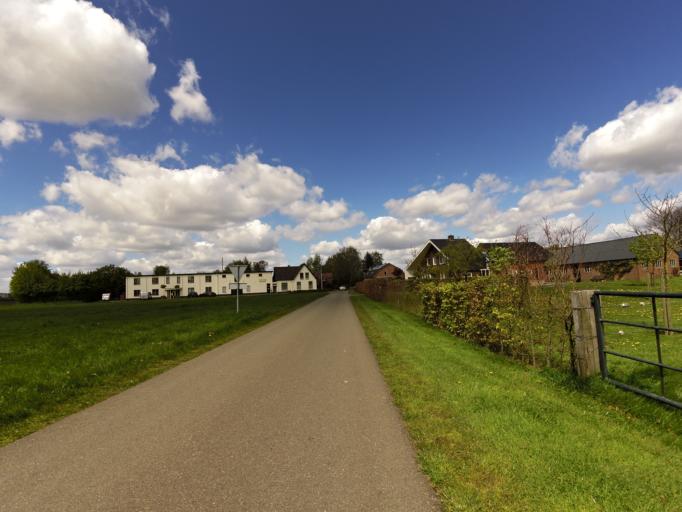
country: NL
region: Gelderland
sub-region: Gemeente Doetinchem
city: Doetinchem
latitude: 51.9408
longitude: 6.2524
